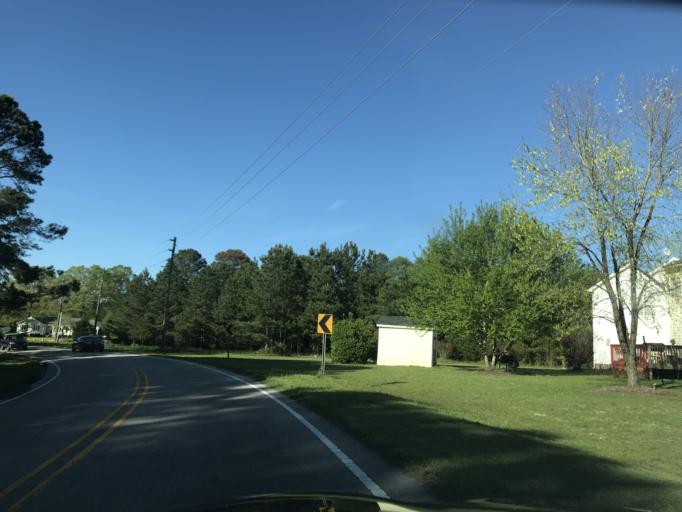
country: US
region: North Carolina
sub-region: Wake County
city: Knightdale
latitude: 35.8192
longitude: -78.5554
